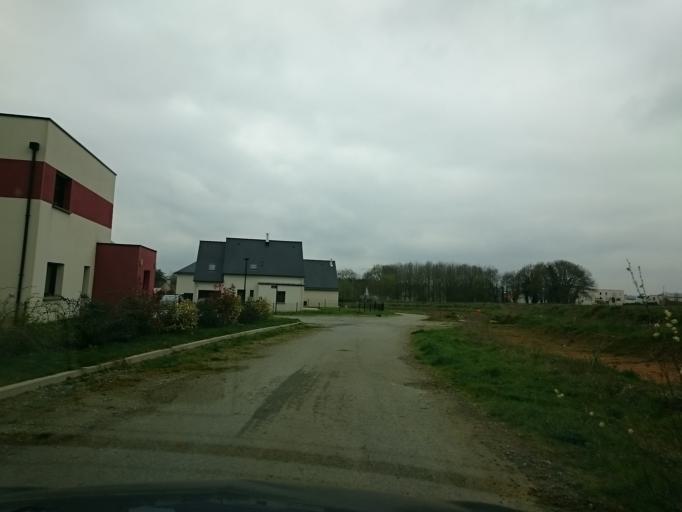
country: FR
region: Brittany
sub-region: Departement d'Ille-et-Vilaine
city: Corps-Nuds
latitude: 47.9852
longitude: -1.5823
